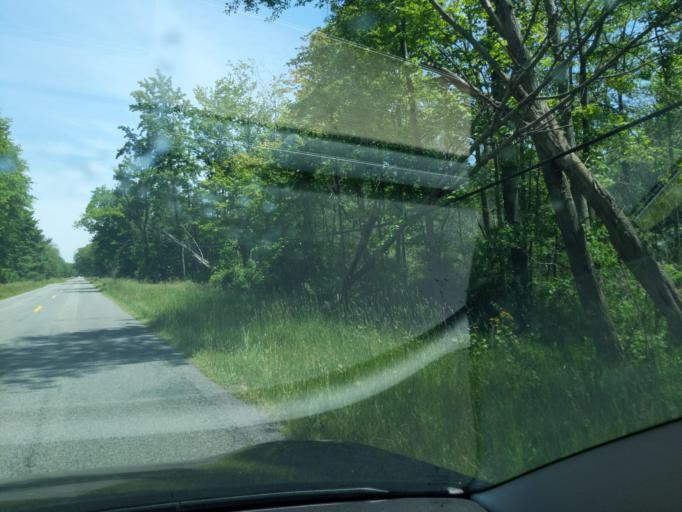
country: US
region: Michigan
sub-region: Muskegon County
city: Montague
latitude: 43.4155
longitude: -86.3850
